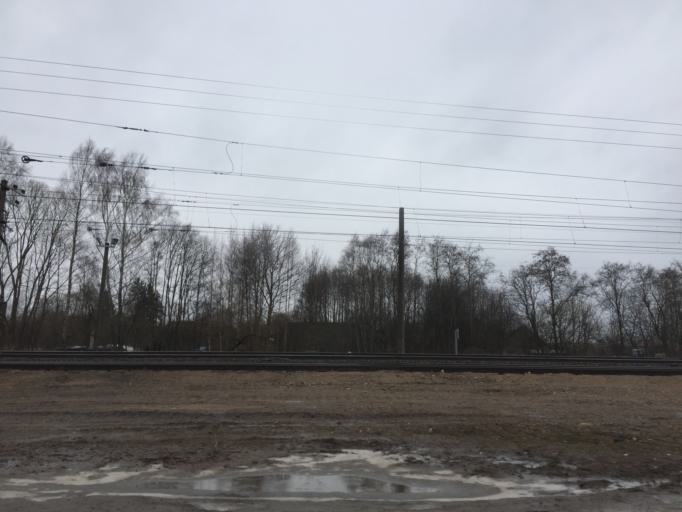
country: LV
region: Lielvarde
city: Lielvarde
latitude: 56.7236
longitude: 24.7991
